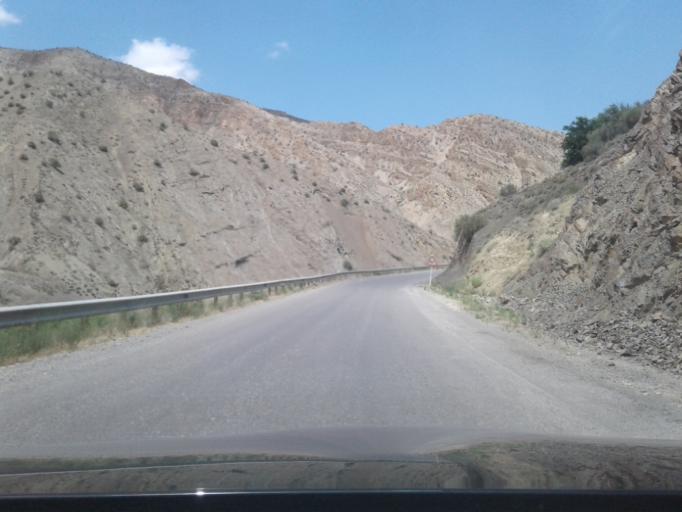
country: TM
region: Ahal
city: Baharly
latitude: 38.5047
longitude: 57.0506
